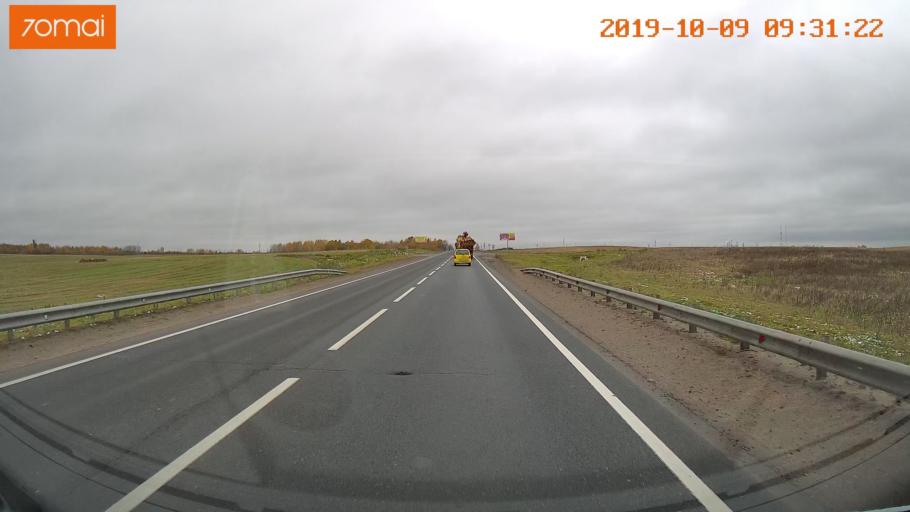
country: RU
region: Vologda
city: Vologda
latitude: 59.1490
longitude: 39.9392
